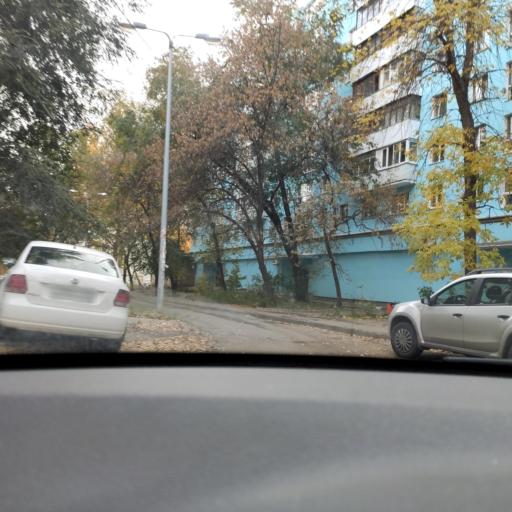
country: RU
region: Samara
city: Samara
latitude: 53.2336
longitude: 50.2146
